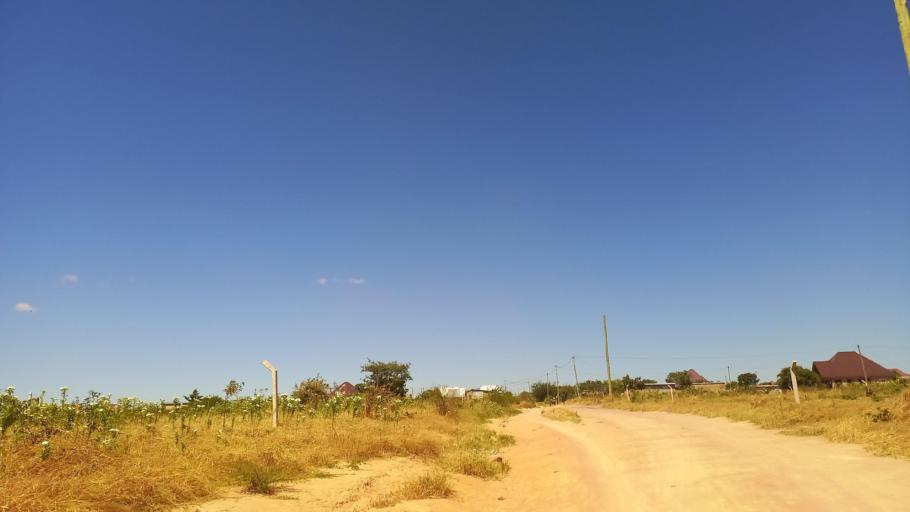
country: TZ
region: Dodoma
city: Dodoma
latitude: -6.1263
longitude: 35.6967
